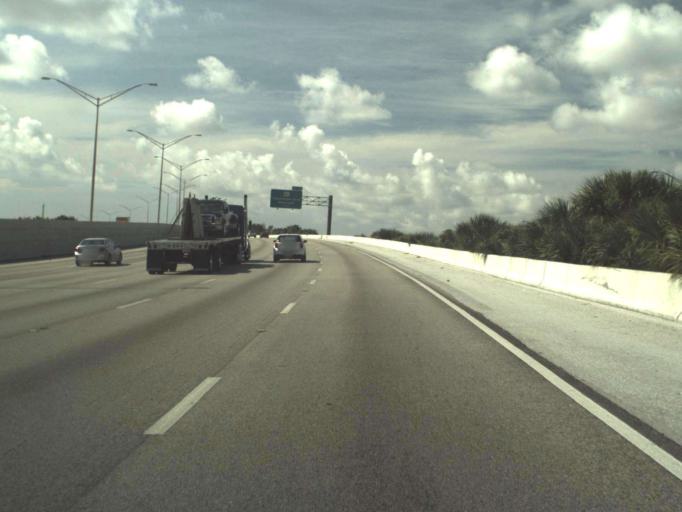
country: US
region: Florida
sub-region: Palm Beach County
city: Schall Circle
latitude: 26.7219
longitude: -80.0913
